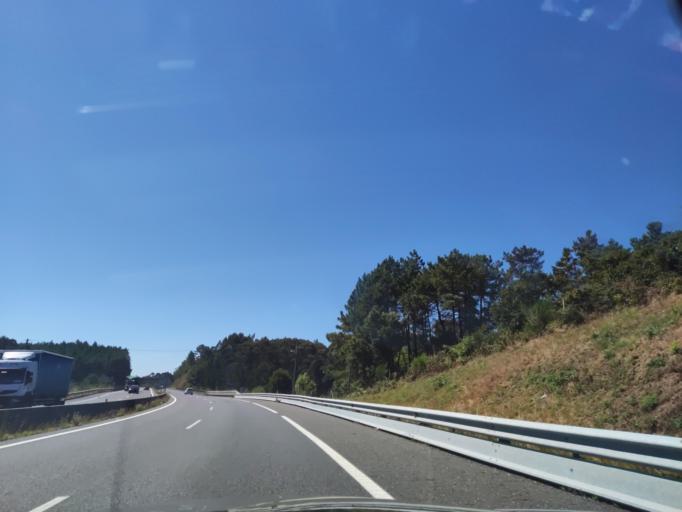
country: ES
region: Galicia
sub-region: Provincia da Coruna
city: Boiro
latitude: 42.6426
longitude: -8.9113
